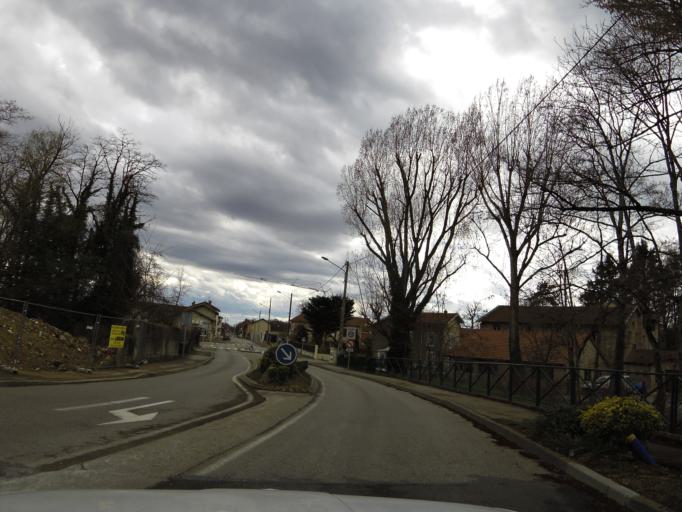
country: FR
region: Rhone-Alpes
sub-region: Departement de l'Ain
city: Meximieux
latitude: 45.9225
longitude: 5.2251
